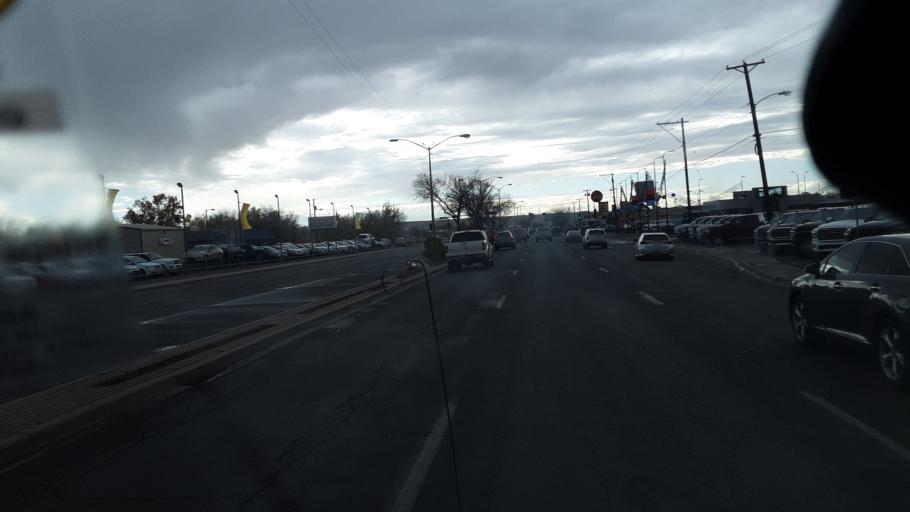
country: US
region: New Mexico
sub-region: San Juan County
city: Farmington
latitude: 36.7488
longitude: -108.1610
